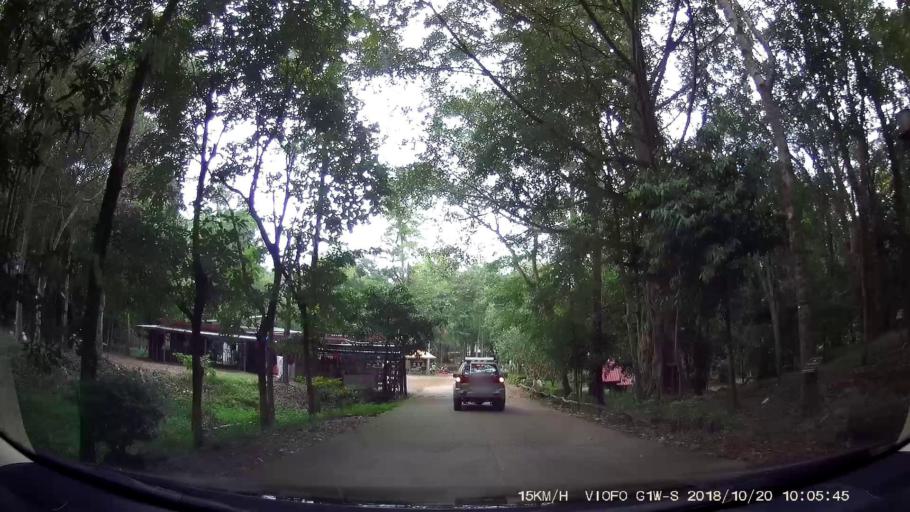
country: TH
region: Chaiyaphum
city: Khon San
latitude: 16.5435
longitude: 101.8516
